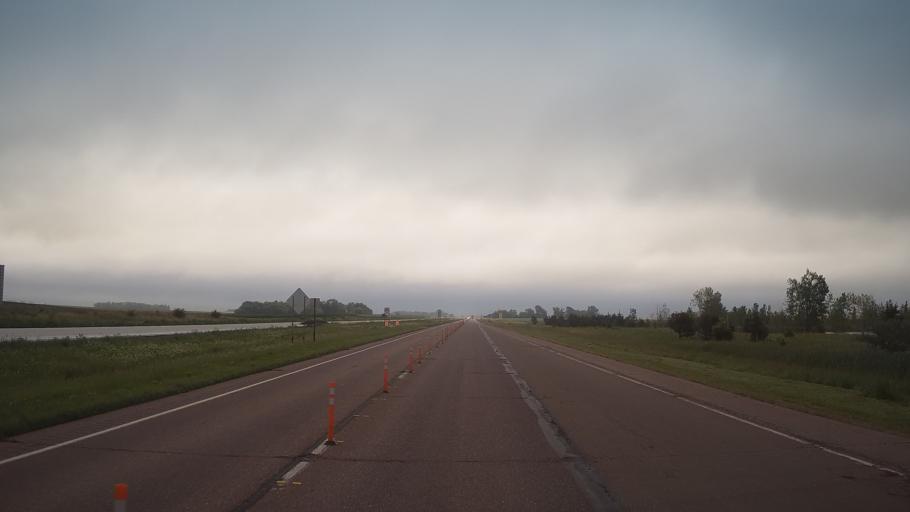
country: US
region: Minnesota
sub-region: Faribault County
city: Winnebago
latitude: 43.6662
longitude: -94.2224
